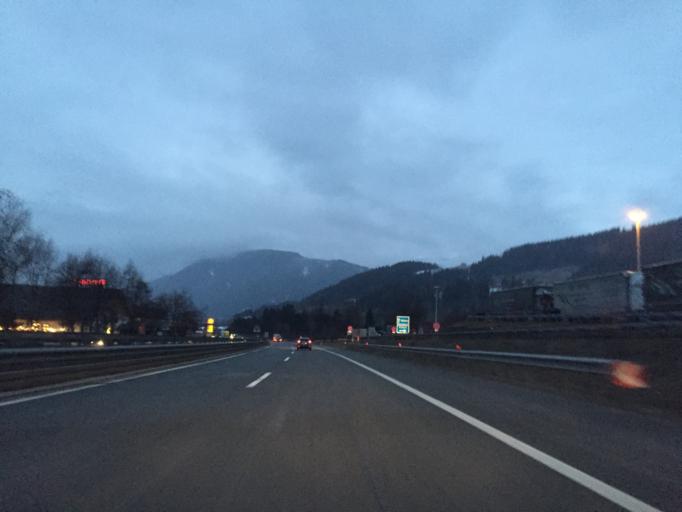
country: AT
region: Salzburg
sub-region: Politischer Bezirk Sankt Johann im Pongau
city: Eben im Pongau
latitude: 47.4209
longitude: 13.3830
